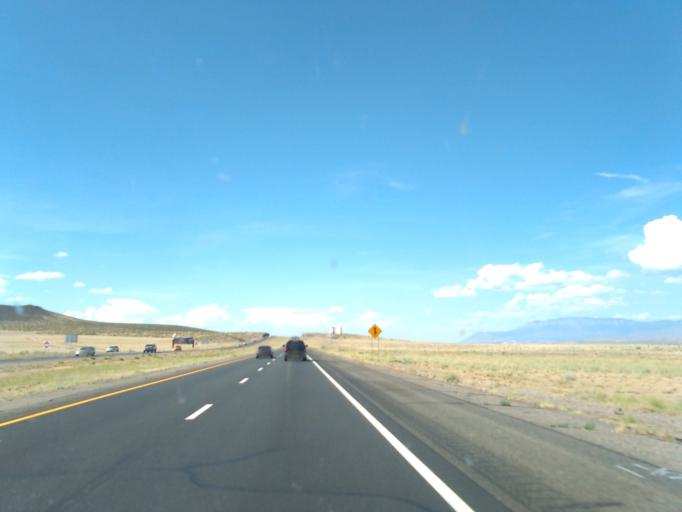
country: US
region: New Mexico
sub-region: Valencia County
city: Bosque Farms
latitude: 34.9061
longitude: -106.7235
